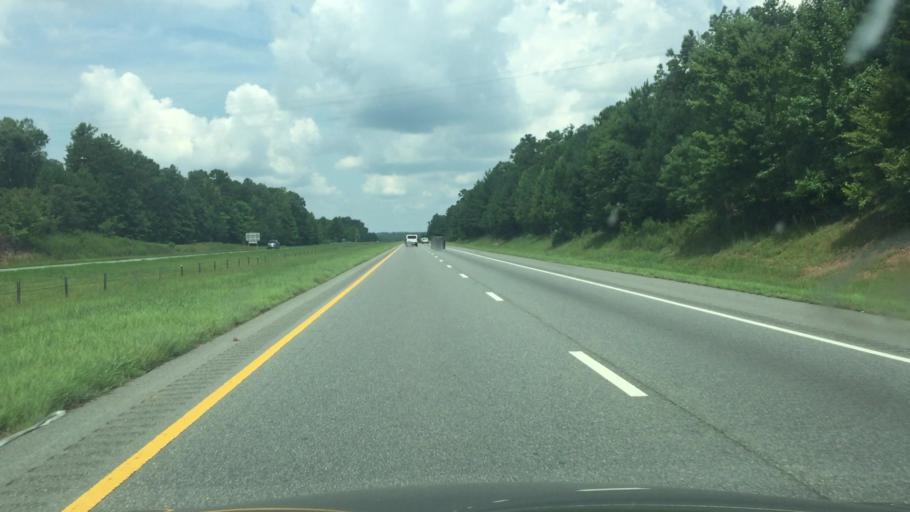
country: US
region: North Carolina
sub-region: Randolph County
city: Asheboro
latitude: 35.5484
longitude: -79.7969
